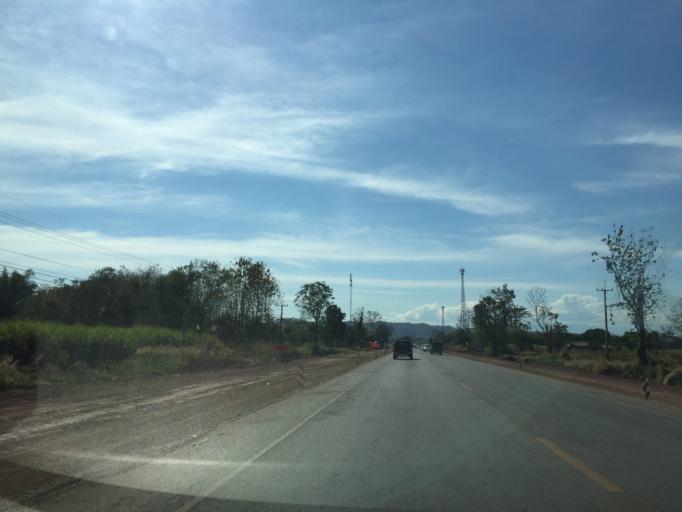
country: TH
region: Loei
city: Erawan
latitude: 17.3019
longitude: 101.8822
